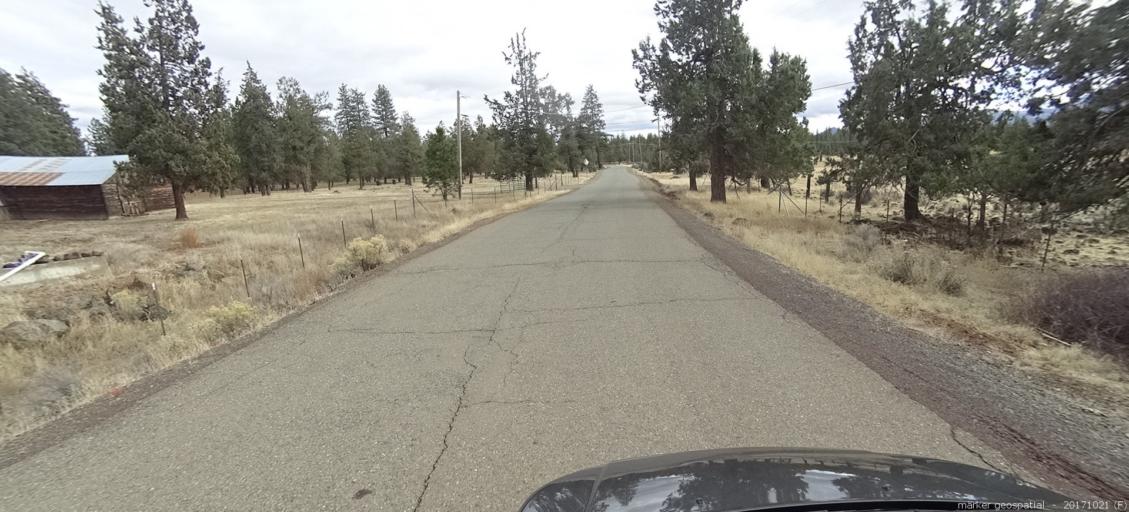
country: US
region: California
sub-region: Shasta County
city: Burney
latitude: 40.9270
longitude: -121.6494
